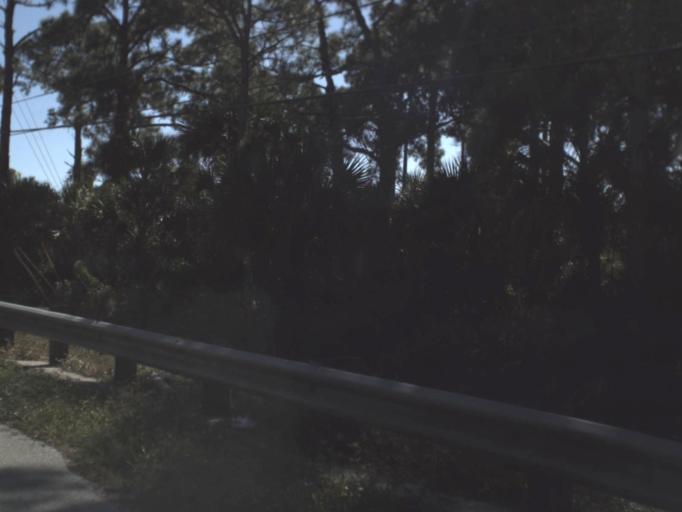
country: US
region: Florida
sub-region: Brevard County
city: Rockledge
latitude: 28.2943
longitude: -80.7146
